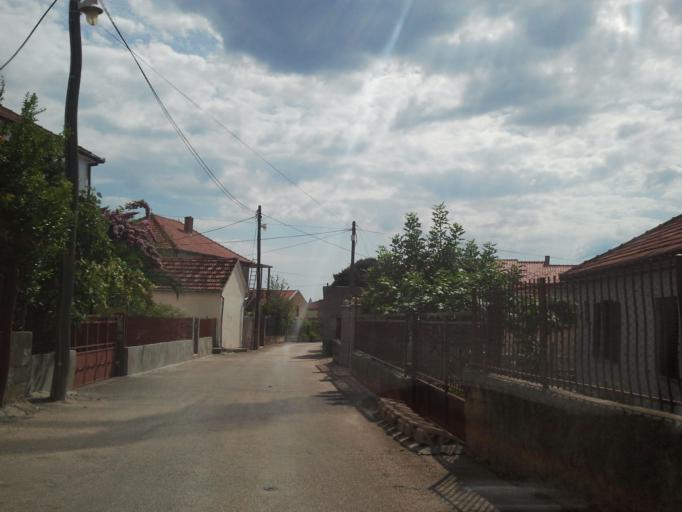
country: HR
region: Zadarska
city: Zadar
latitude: 44.1198
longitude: 15.2496
